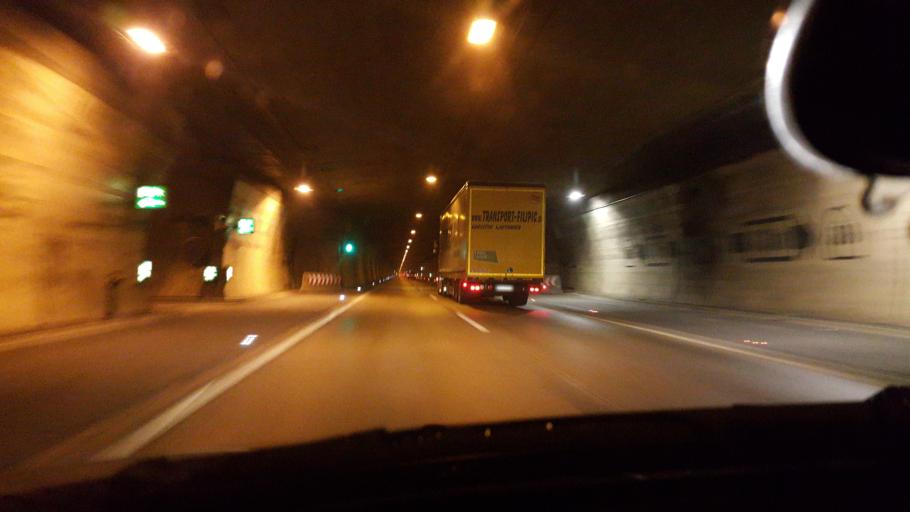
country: AT
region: Styria
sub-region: Graz Stadt
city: Wetzelsdorf
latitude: 47.0649
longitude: 15.3942
